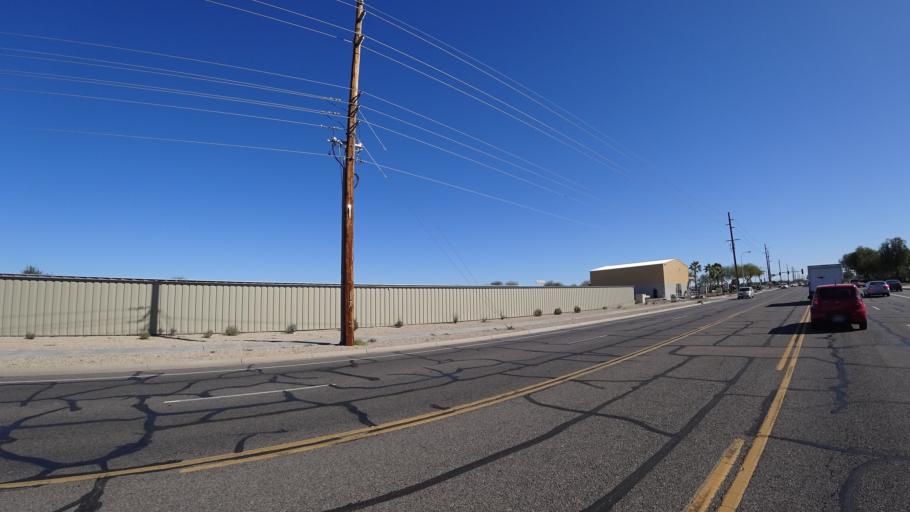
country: US
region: Arizona
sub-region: Maricopa County
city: Sun Lakes
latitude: 33.2185
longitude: -111.8434
